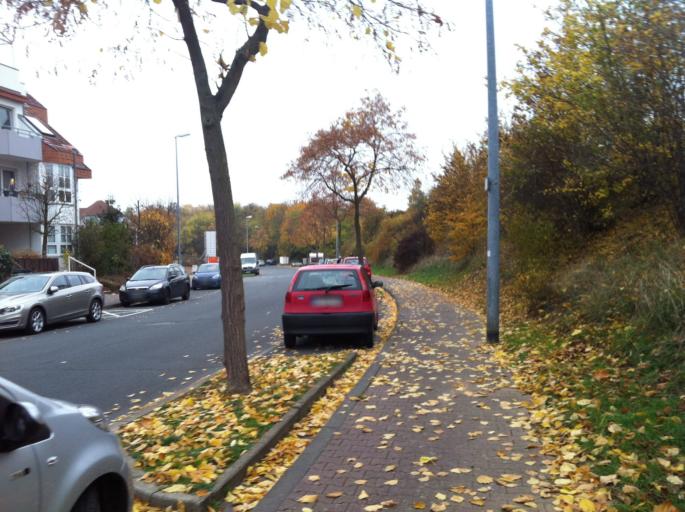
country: DE
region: Rheinland-Pfalz
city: Budenheim
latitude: 49.9987
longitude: 8.1830
